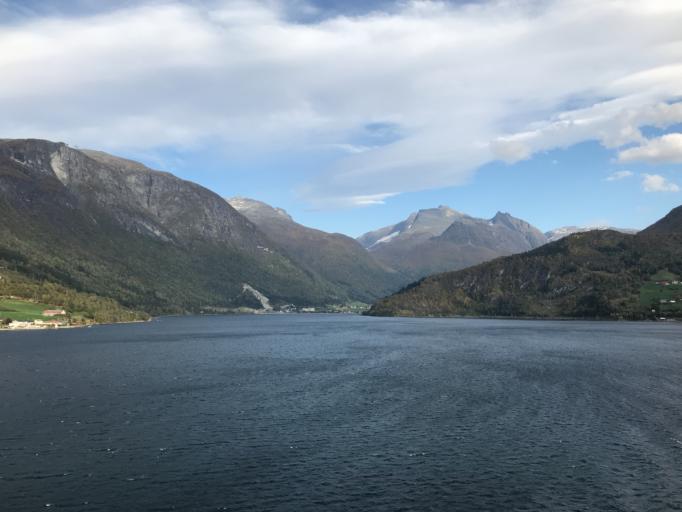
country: NO
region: Sogn og Fjordane
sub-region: Stryn
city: Stryn
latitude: 61.8638
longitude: 6.7808
